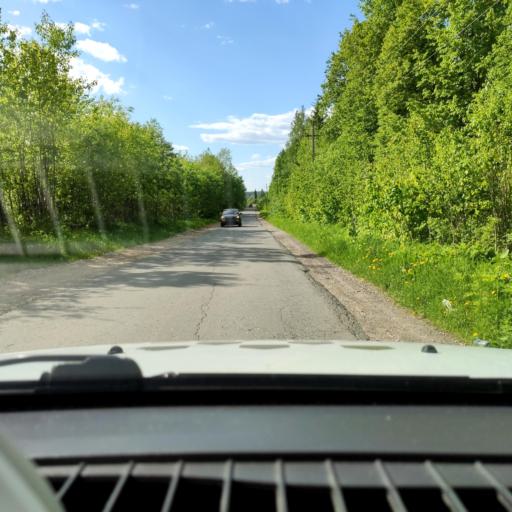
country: RU
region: Perm
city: Novyye Lyady
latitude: 58.0410
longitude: 56.6231
